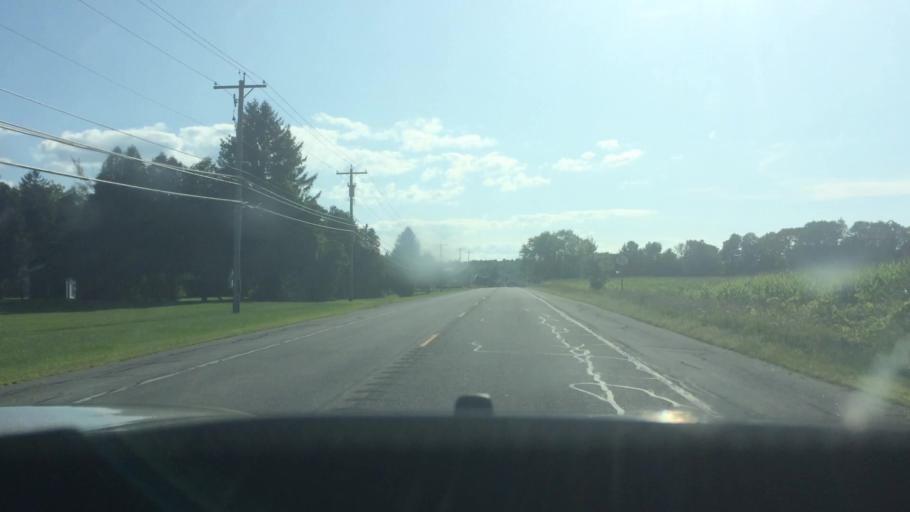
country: US
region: New York
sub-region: Franklin County
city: Malone
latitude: 44.8247
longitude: -74.3490
